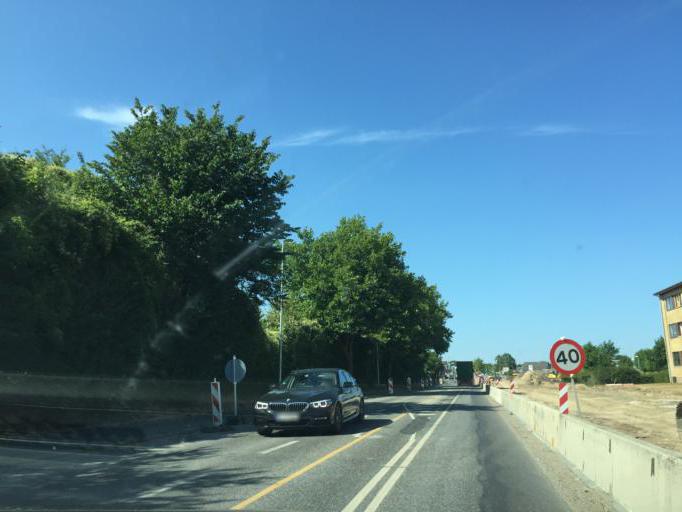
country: DK
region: South Denmark
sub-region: Odense Kommune
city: Odense
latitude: 55.4049
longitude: 10.3401
